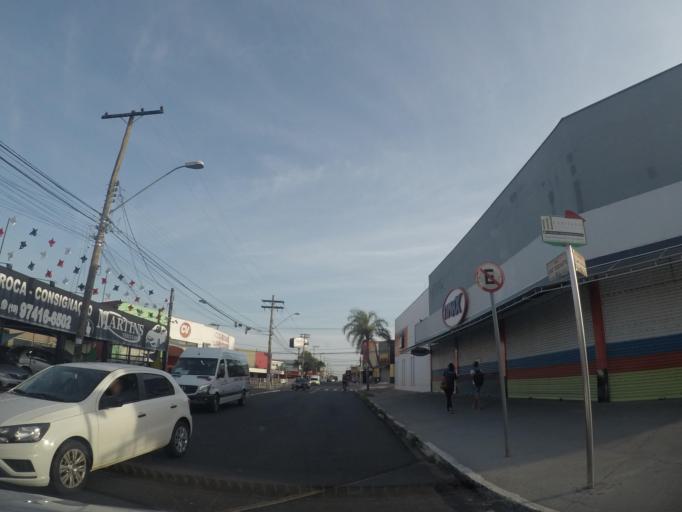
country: BR
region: Sao Paulo
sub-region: Hortolandia
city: Hortolandia
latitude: -22.8518
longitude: -47.1922
